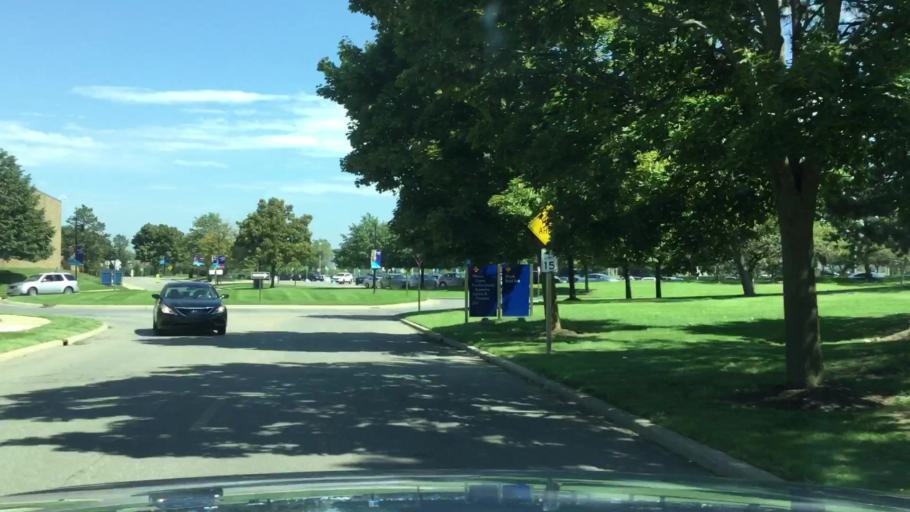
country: US
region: Michigan
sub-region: Oakland County
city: West Bloomfield Township
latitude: 42.5429
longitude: -83.4047
